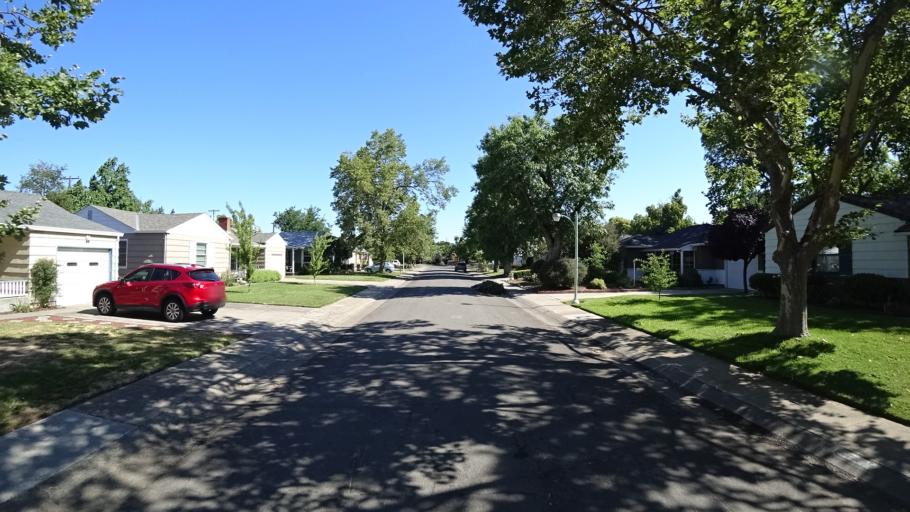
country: US
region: California
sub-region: Sacramento County
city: Parkway
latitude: 38.5267
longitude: -121.4930
